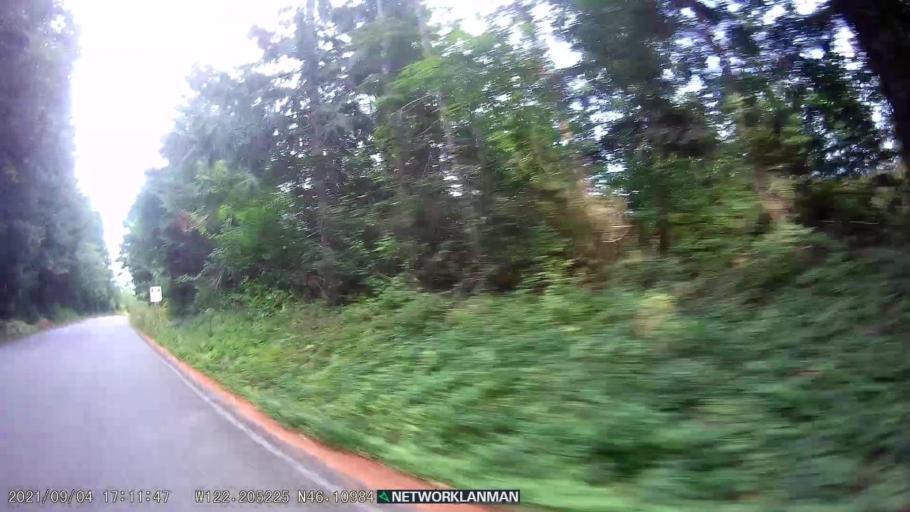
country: US
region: Washington
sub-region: Clark County
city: Amboy
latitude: 46.1100
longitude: -122.2053
